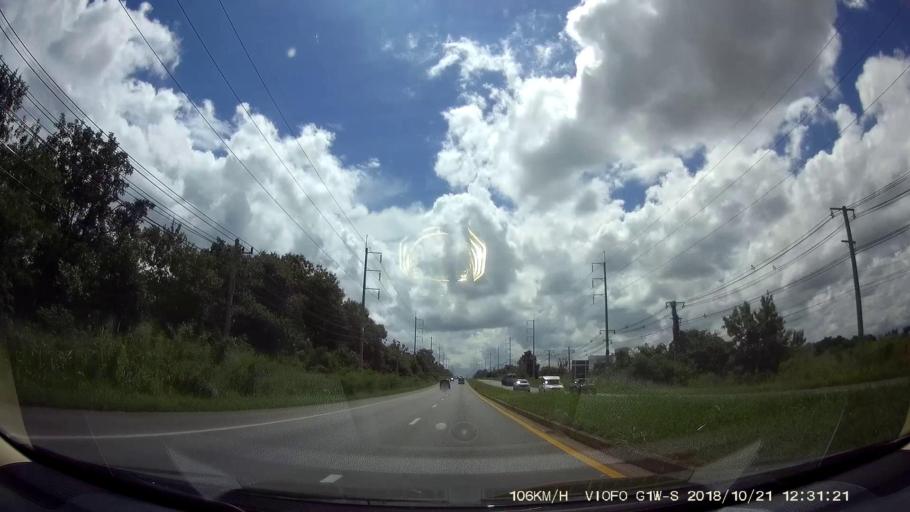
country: TH
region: Nakhon Ratchasima
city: Dan Khun Thot
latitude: 15.1579
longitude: 101.7353
